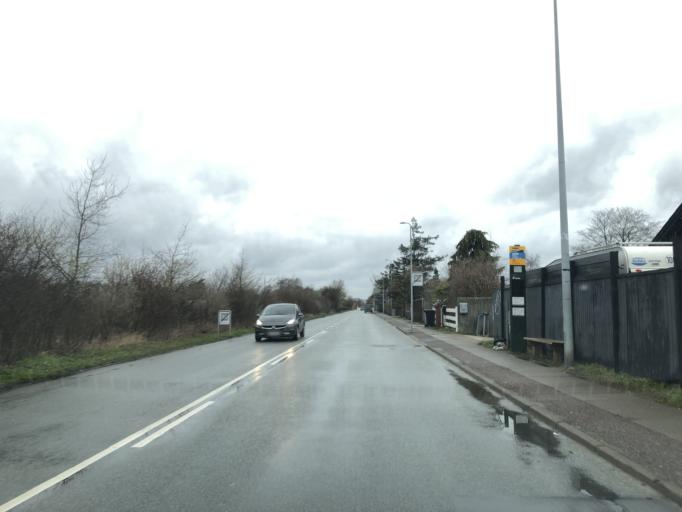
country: DK
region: Capital Region
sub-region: Dragor Kommune
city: Dragor
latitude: 55.5842
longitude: 12.6364
